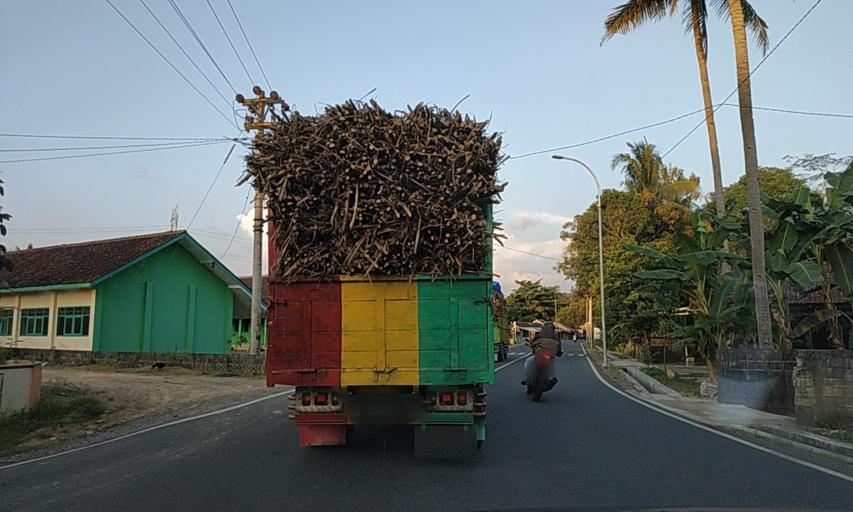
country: ID
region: Daerah Istimewa Yogyakarta
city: Srandakan
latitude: -7.8839
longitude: 110.0456
